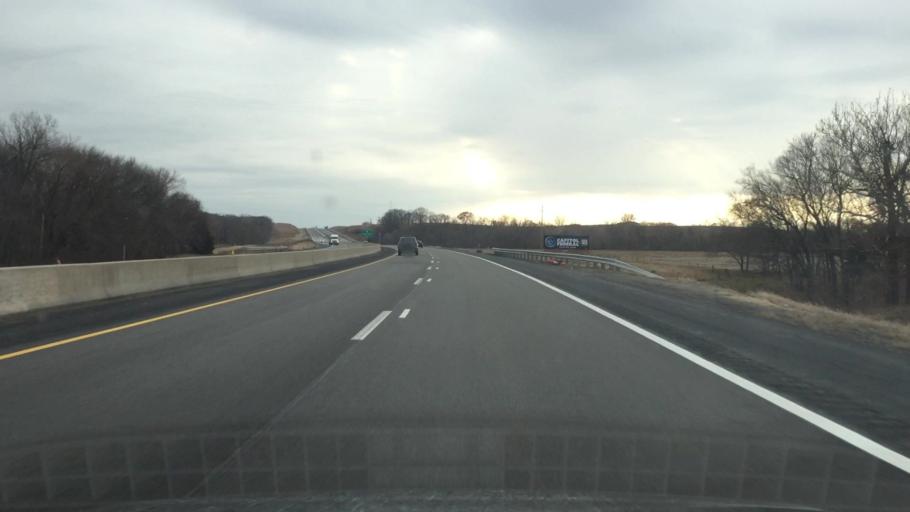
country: US
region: Kansas
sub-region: Osage County
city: Osage City
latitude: 38.6679
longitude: -96.0161
